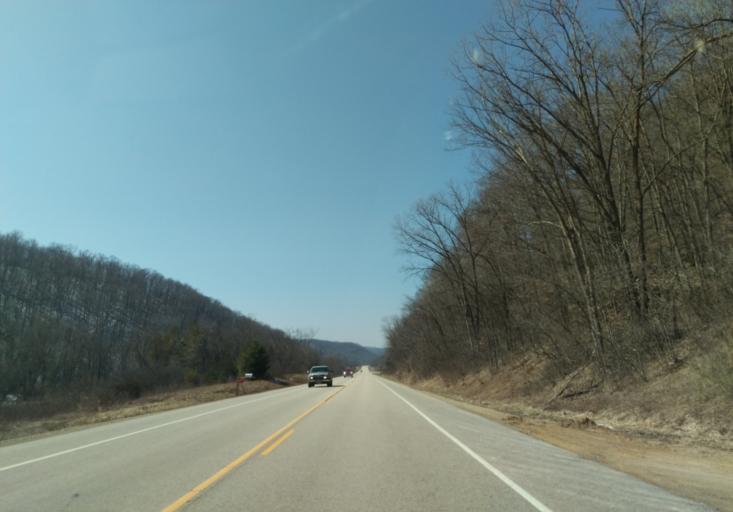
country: US
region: Wisconsin
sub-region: Vernon County
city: Viroqua
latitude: 43.4486
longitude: -90.7208
